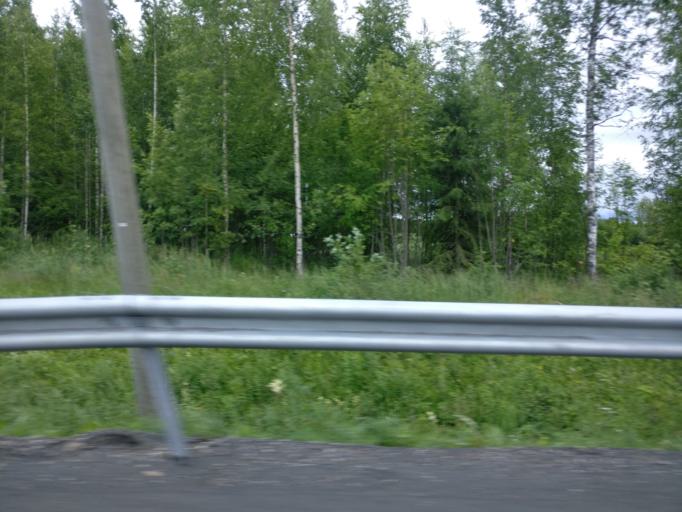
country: FI
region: Northern Savo
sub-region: Varkaus
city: Leppaevirta
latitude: 62.6089
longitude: 27.6231
